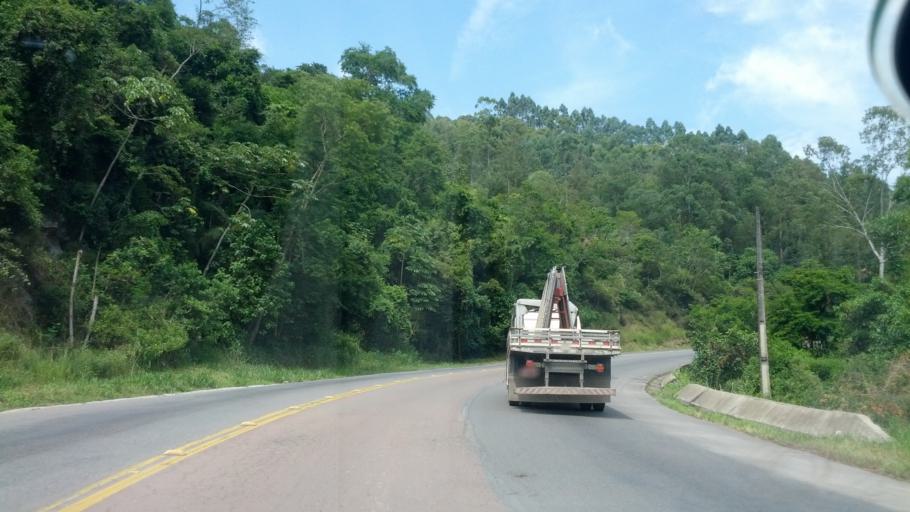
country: BR
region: Santa Catarina
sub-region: Ibirama
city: Ibirama
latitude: -27.0915
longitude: -49.5207
